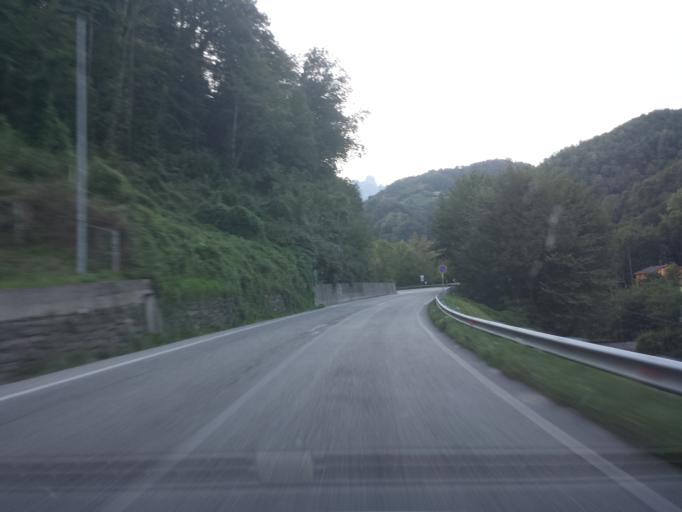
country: IT
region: Veneto
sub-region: Provincia di Vicenza
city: Recoaro Terme
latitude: 45.7023
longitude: 11.2450
